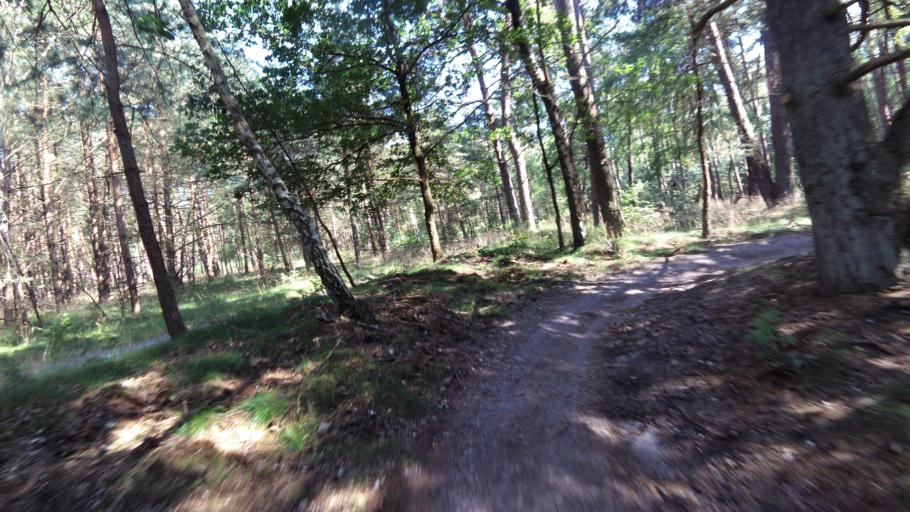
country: NL
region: Gelderland
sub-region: Gemeente Arnhem
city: Gulden Bodem
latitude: 52.0222
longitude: 5.9165
